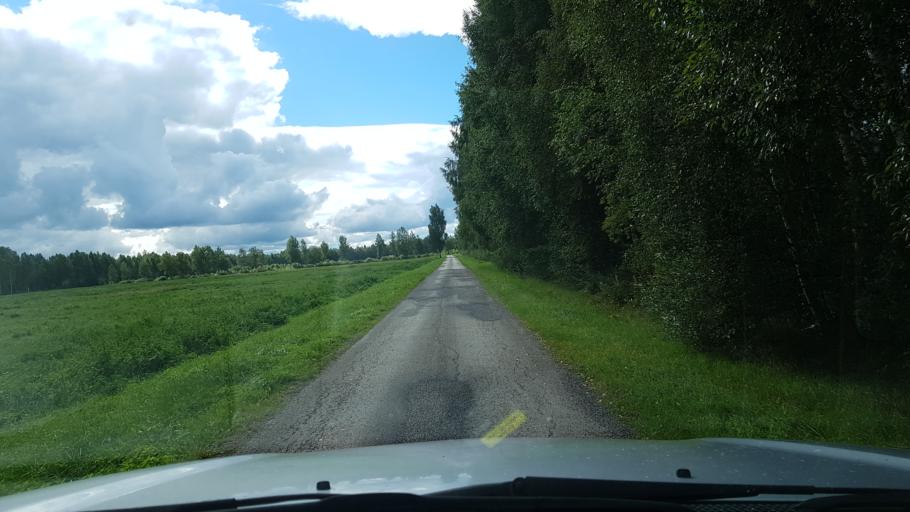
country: EE
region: Harju
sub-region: Raasiku vald
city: Arukula
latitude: 59.2999
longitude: 25.0574
